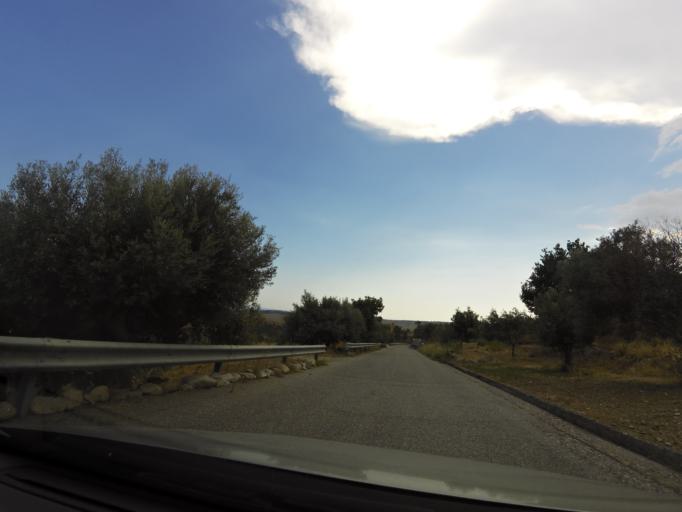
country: IT
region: Calabria
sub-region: Provincia di Reggio Calabria
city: Camini
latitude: 38.4291
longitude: 16.5146
